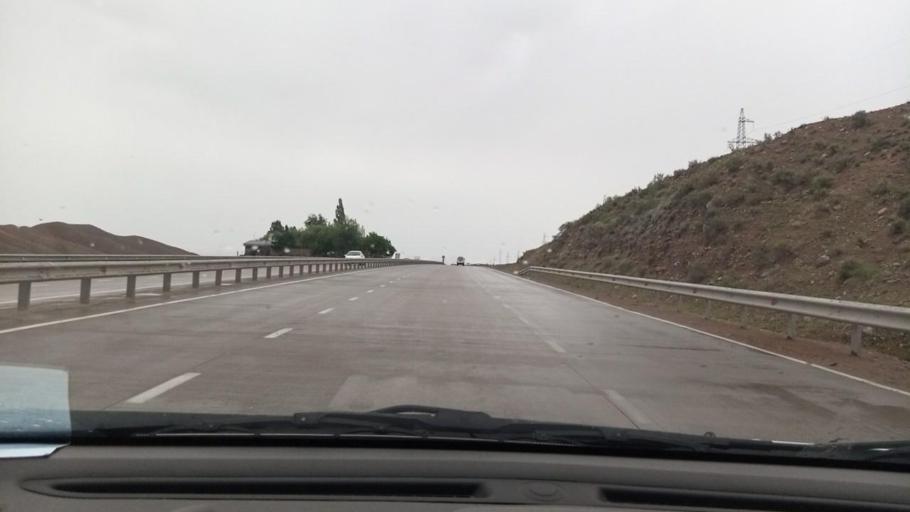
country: UZ
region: Namangan
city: Pop Shahri
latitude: 40.9423
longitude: 70.6882
